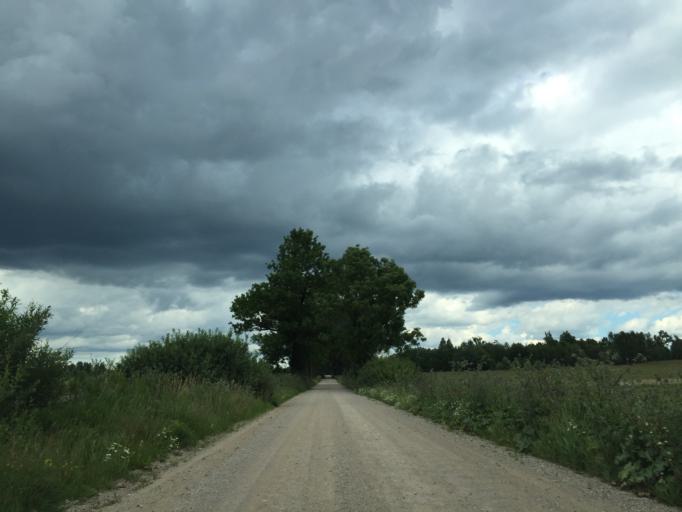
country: LV
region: Malpils
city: Malpils
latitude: 56.9202
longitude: 25.0040
